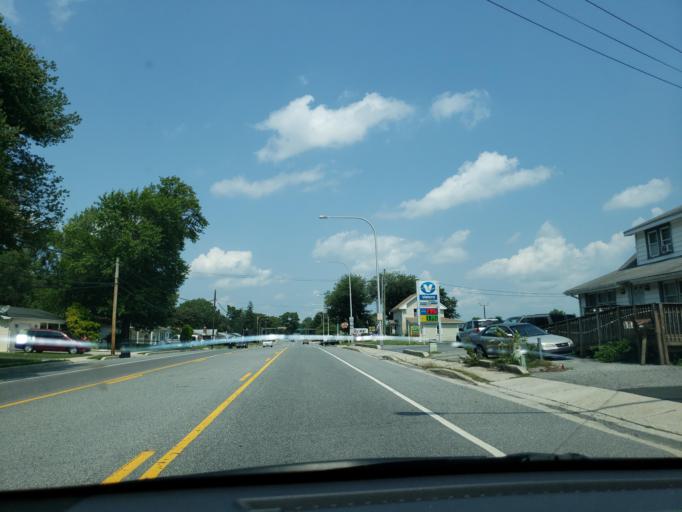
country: US
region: Delaware
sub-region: Kent County
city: Rodney Village
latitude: 39.1309
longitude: -75.5304
